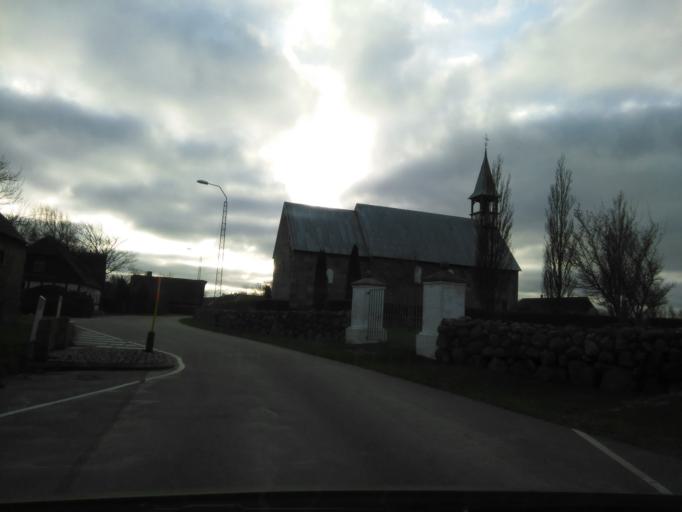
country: DK
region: Central Jutland
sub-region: Arhus Kommune
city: Framlev
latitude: 56.1715
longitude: 10.0421
